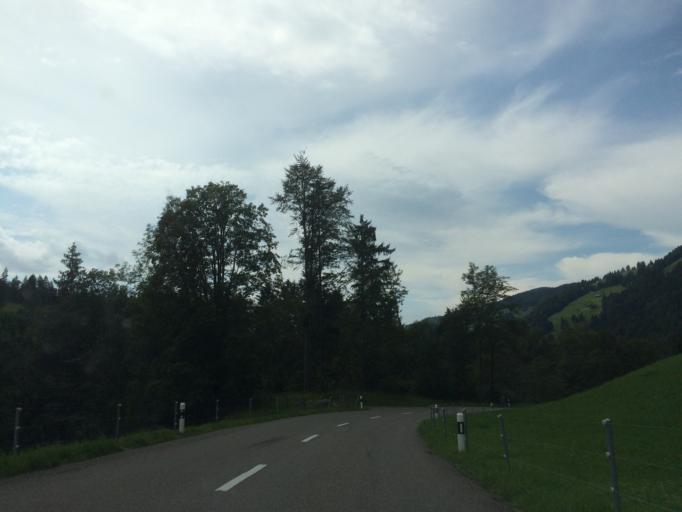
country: CH
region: Appenzell Ausserrhoden
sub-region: Bezirk Hinterland
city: Urnasch
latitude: 47.2432
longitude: 9.2643
